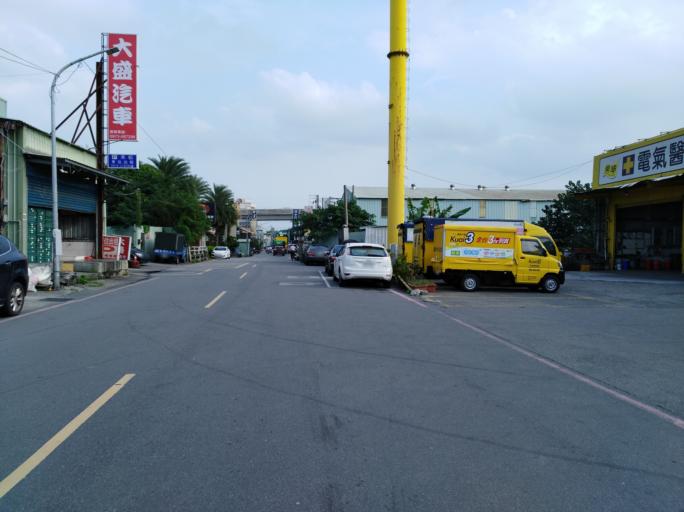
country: TW
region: Taipei
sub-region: Taipei
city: Banqiao
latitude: 25.0378
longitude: 121.4255
